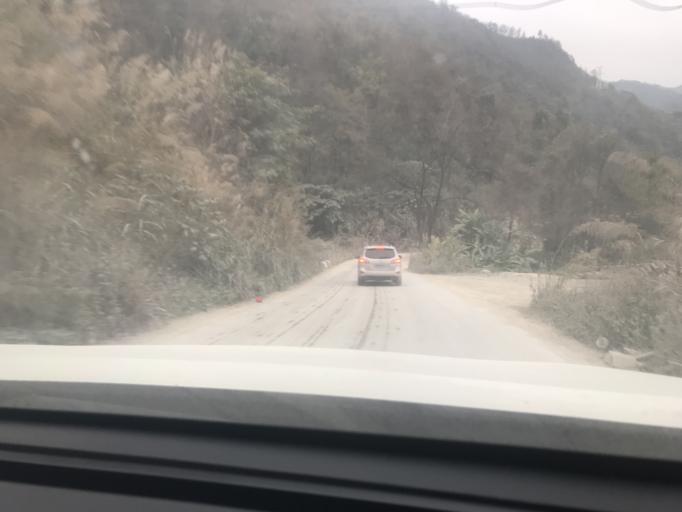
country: CN
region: Guangxi Zhuangzu Zizhiqu
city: Xinzhou
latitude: 24.9925
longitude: 105.8233
